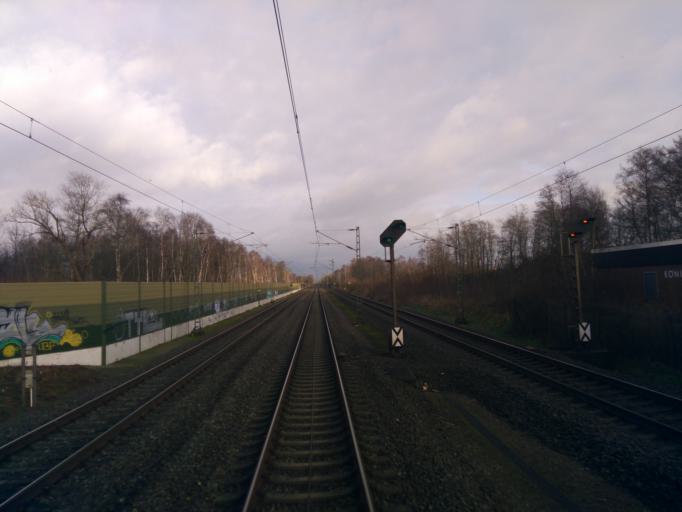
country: DE
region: Lower Saxony
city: Konigsmoor
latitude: 53.2311
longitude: 9.6436
